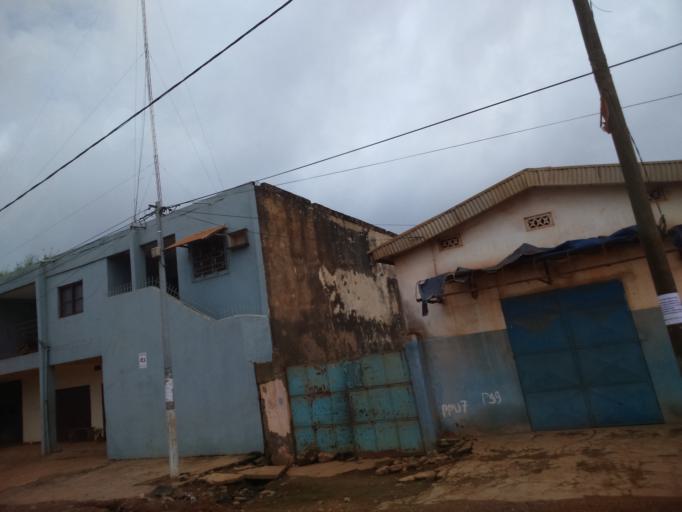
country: CI
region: Moyen-Comoe
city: Abengourou
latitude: 6.7265
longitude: -3.4995
